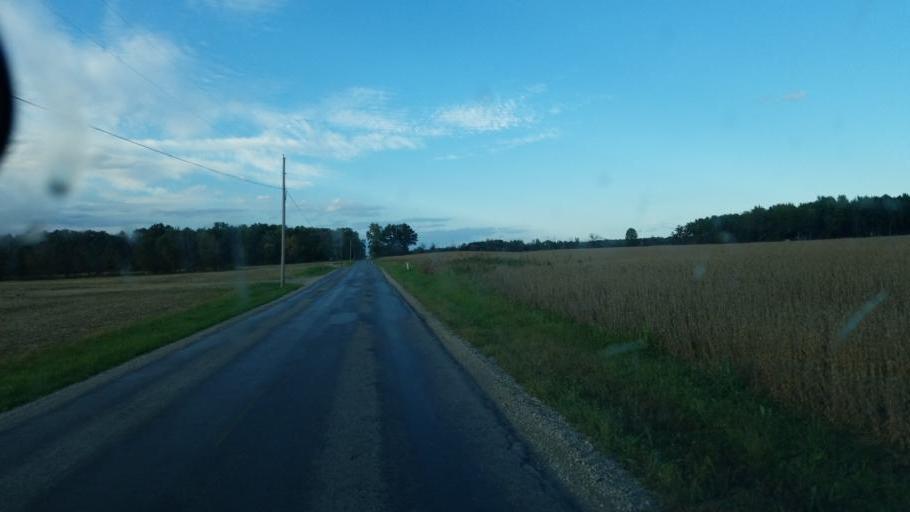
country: US
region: Ohio
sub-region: Franklin County
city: New Albany
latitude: 40.0529
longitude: -82.7555
